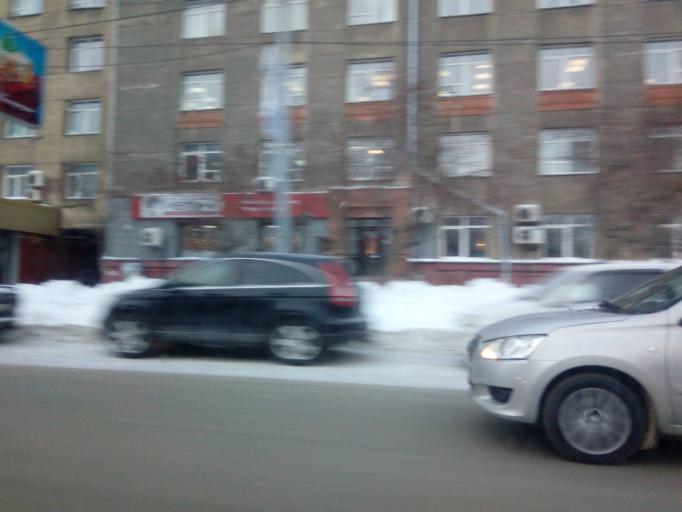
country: RU
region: Novosibirsk
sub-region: Novosibirskiy Rayon
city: Novosibirsk
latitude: 55.0318
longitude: 82.9121
